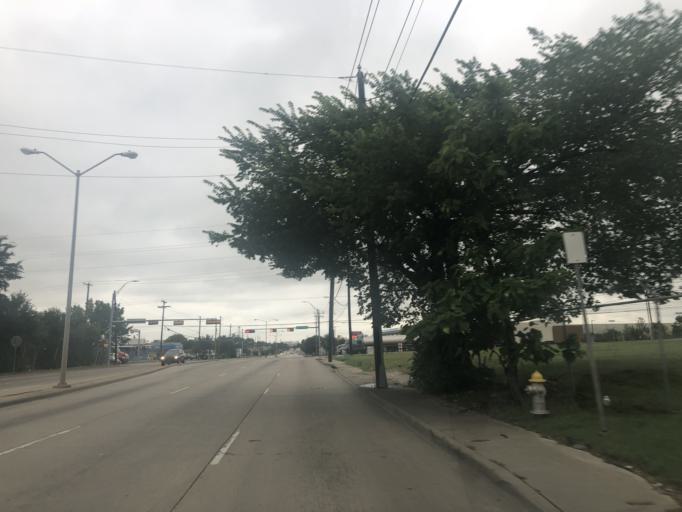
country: US
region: Texas
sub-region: Dallas County
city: Cockrell Hill
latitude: 32.7778
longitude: -96.8737
